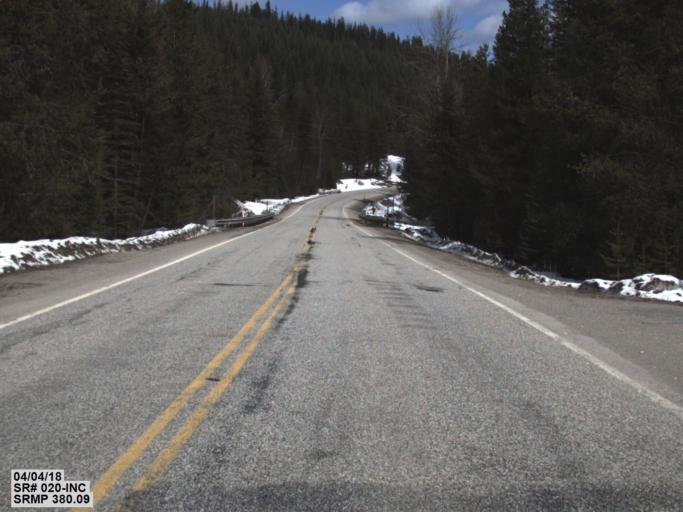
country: US
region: Washington
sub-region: Stevens County
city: Colville
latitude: 48.6250
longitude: -117.5451
